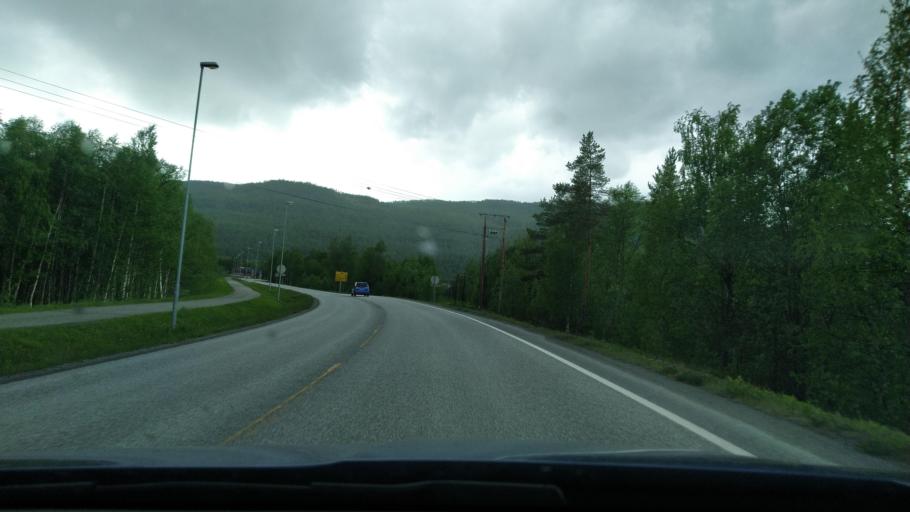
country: NO
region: Troms
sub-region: Malselv
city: Moen
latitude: 69.0089
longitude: 18.5066
